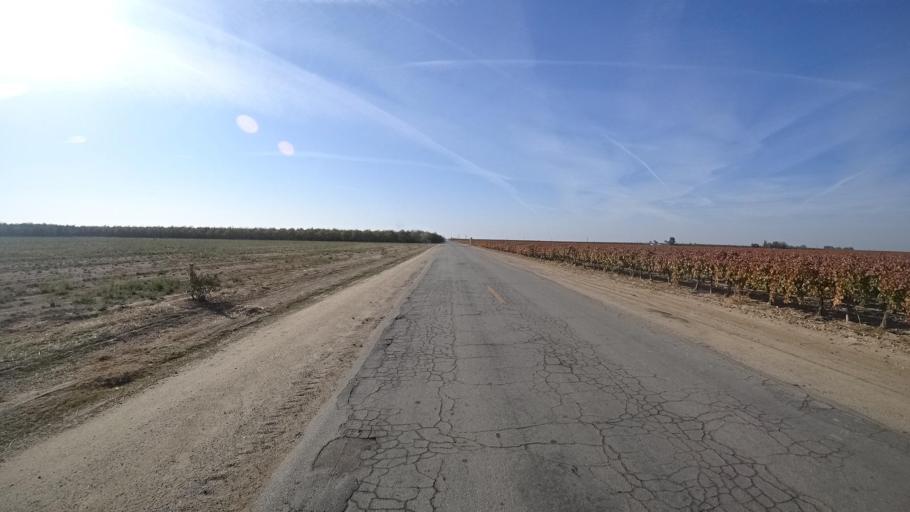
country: US
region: California
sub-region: Kern County
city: McFarland
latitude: 35.7032
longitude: -119.3056
